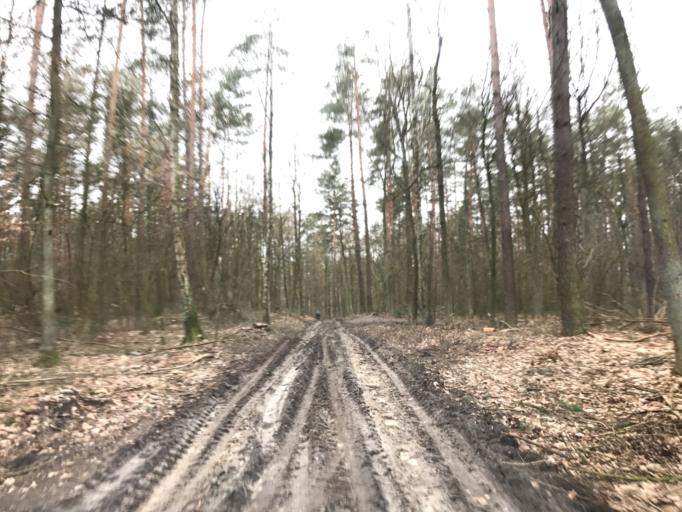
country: PL
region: Kujawsko-Pomorskie
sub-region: Powiat brodnicki
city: Gorzno
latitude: 53.2186
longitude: 19.6475
